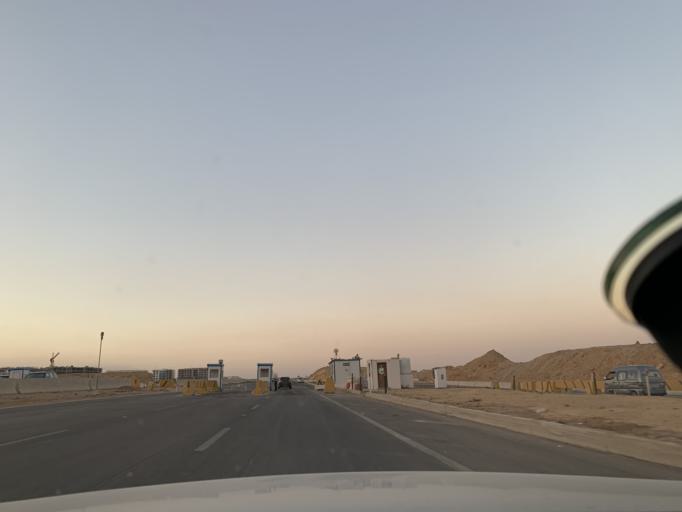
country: EG
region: Muhafazat al Qahirah
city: Halwan
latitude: 29.9618
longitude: 31.5465
